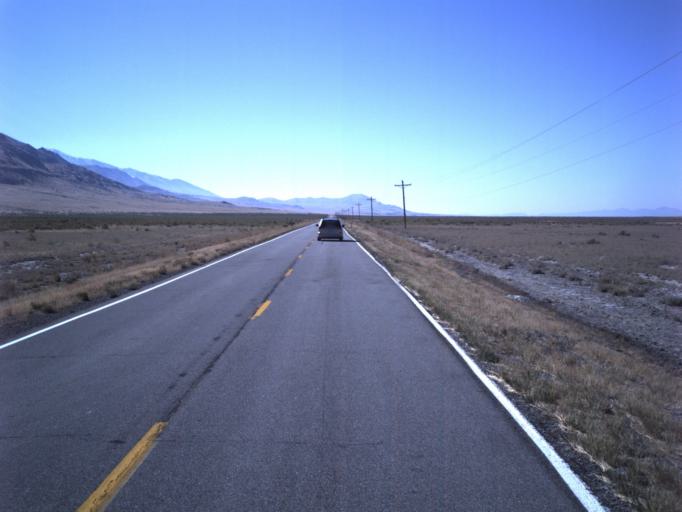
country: US
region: Utah
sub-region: Tooele County
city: Grantsville
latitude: 40.7278
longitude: -112.6582
